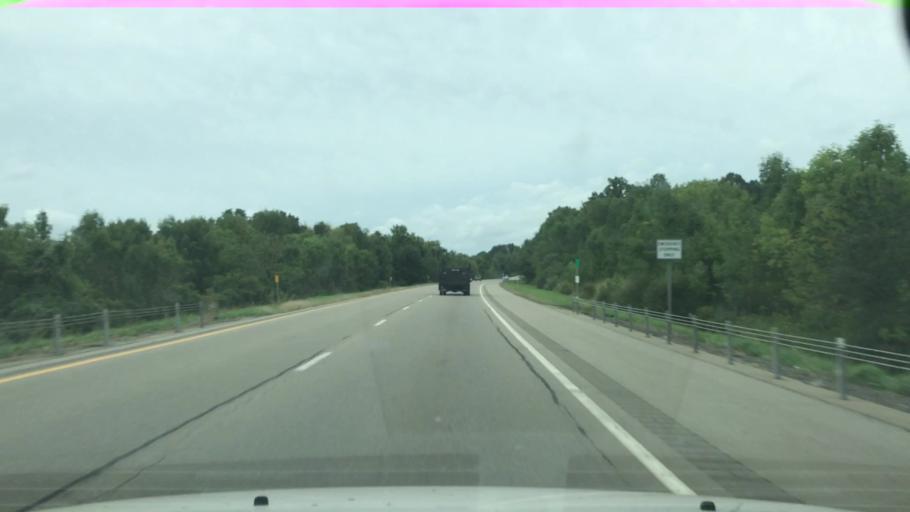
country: US
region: New York
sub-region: Erie County
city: North Boston
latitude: 42.6615
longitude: -78.7697
